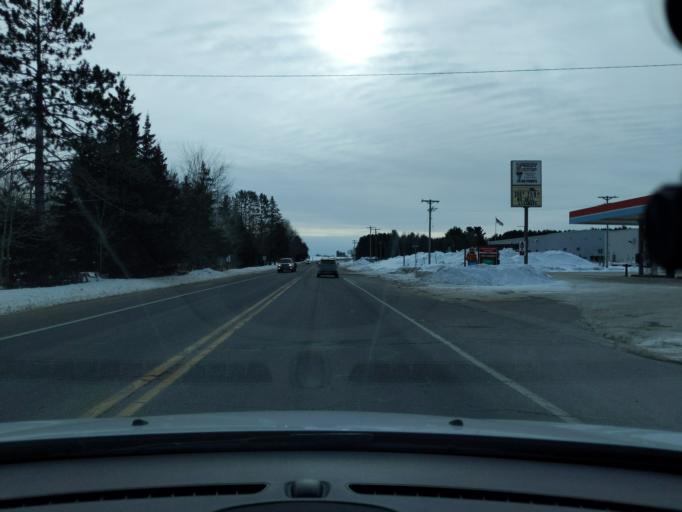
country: US
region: Wisconsin
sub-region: Barron County
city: Cumberland
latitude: 45.6355
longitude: -91.9926
